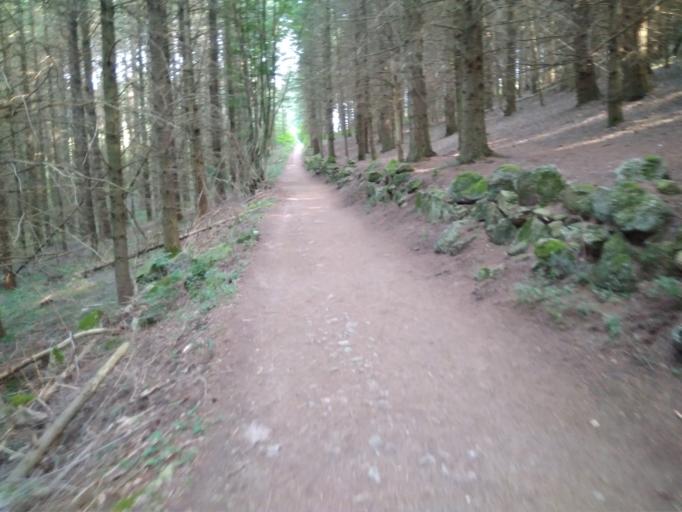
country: FR
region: Auvergne
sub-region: Departement de l'Allier
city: Le Mayet-de-Montagne
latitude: 46.1253
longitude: 3.7629
